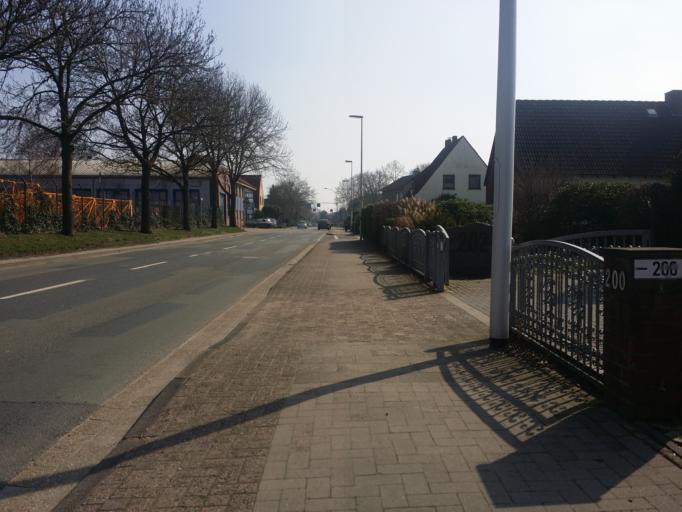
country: DE
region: Lower Saxony
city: Delmenhorst
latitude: 53.0196
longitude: 8.6442
